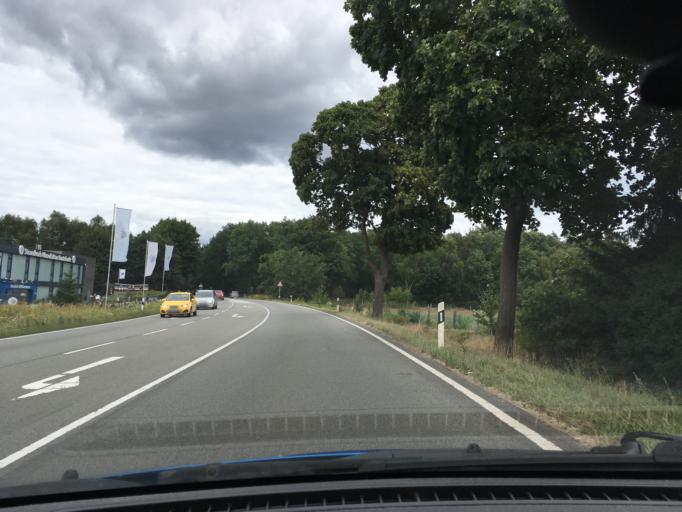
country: DE
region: Lower Saxony
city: Neu Wulmstorf
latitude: 53.4519
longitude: 9.7626
